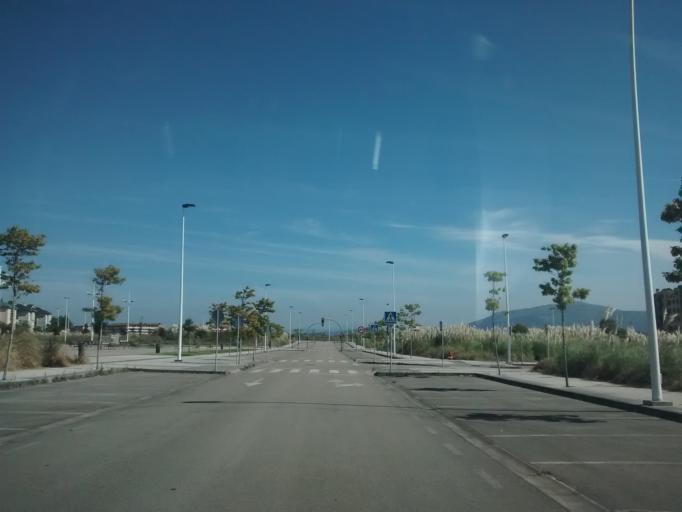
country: ES
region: Cantabria
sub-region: Provincia de Cantabria
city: Camargo
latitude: 43.4401
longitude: -3.8543
